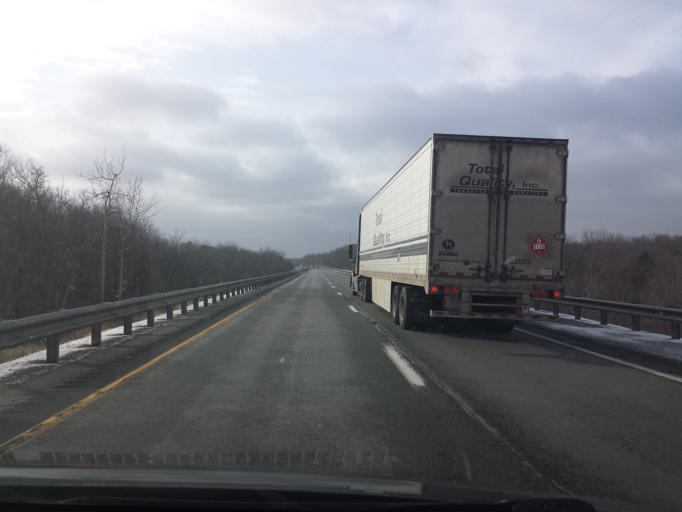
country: US
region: Pennsylvania
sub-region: Monroe County
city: Emerald Lakes
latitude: 41.0728
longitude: -75.4111
